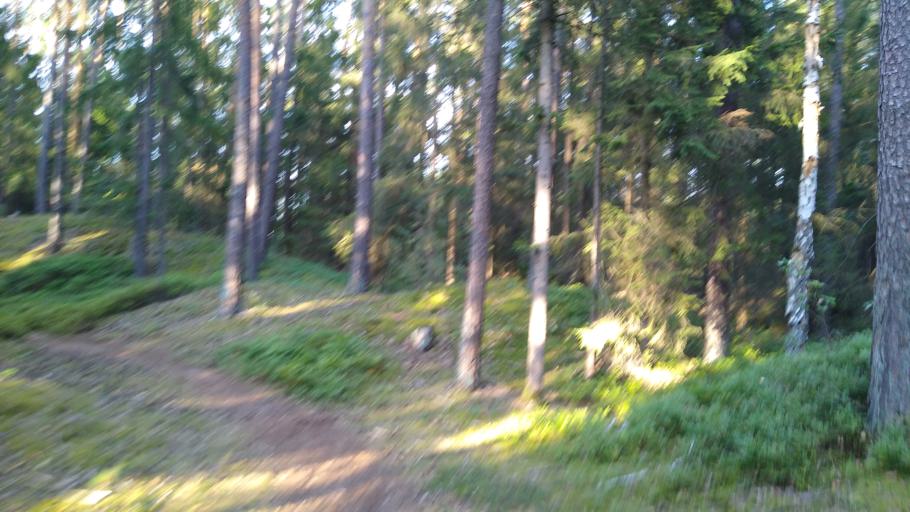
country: DE
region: Bavaria
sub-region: Regierungsbezirk Mittelfranken
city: Zirndorf
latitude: 49.4653
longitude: 10.9363
